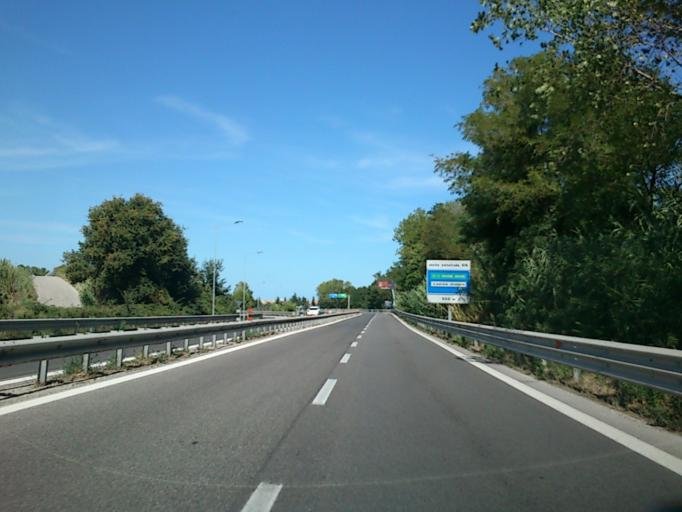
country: IT
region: The Marches
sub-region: Provincia di Pesaro e Urbino
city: Rosciano
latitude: 43.8163
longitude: 13.0173
